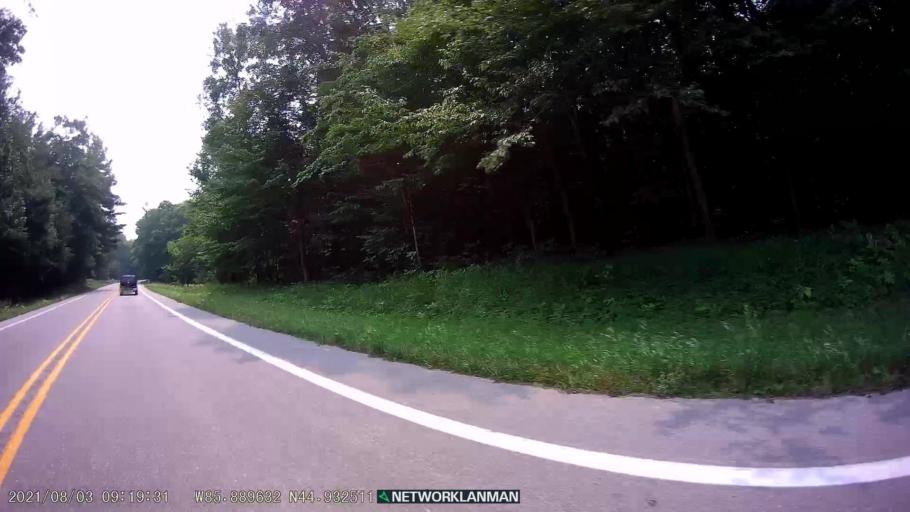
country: US
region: Michigan
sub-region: Leelanau County
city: Leland
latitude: 44.9324
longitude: -85.8894
